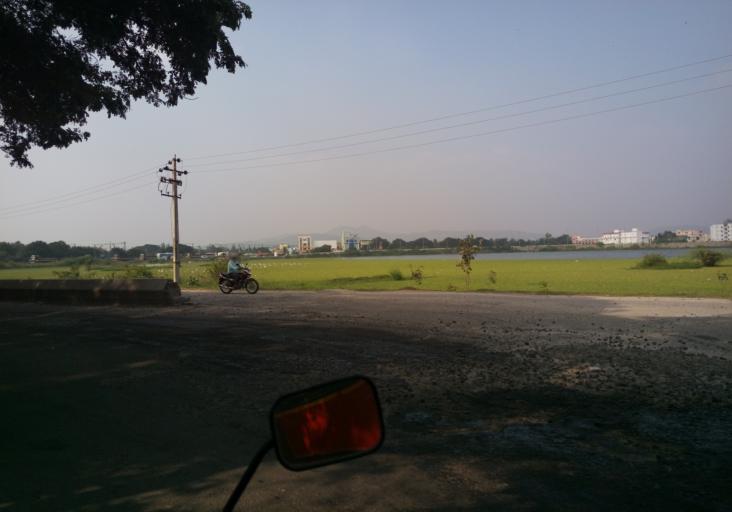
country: IN
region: Andhra Pradesh
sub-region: Chittoor
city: Chittoor
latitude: 13.2202
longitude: 79.1065
